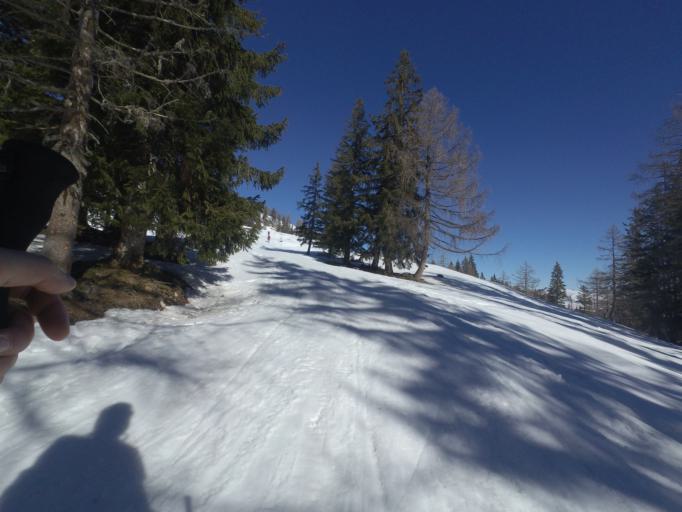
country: AT
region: Upper Austria
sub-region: Politischer Bezirk Gmunden
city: Sankt Wolfgang im Salzkammergut
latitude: 47.6571
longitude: 13.3930
